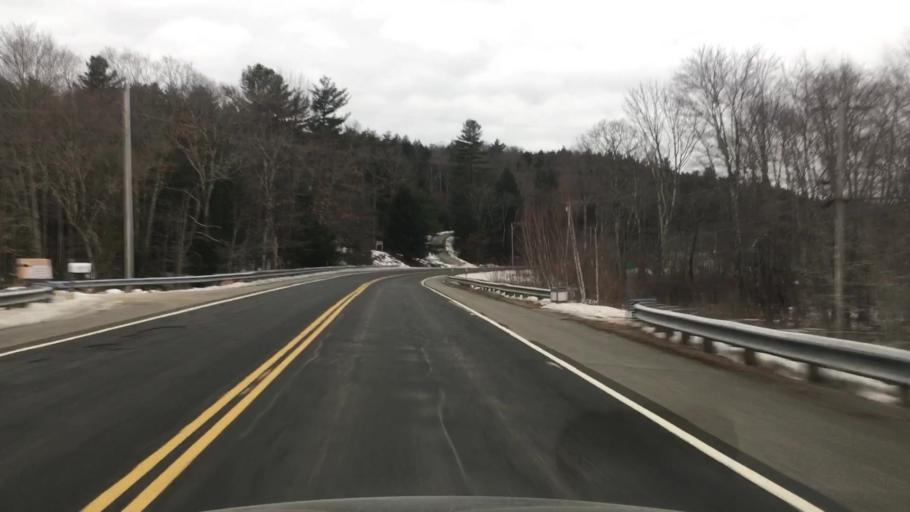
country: US
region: New Hampshire
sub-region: Merrimack County
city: Henniker
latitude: 43.2356
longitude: -71.9114
